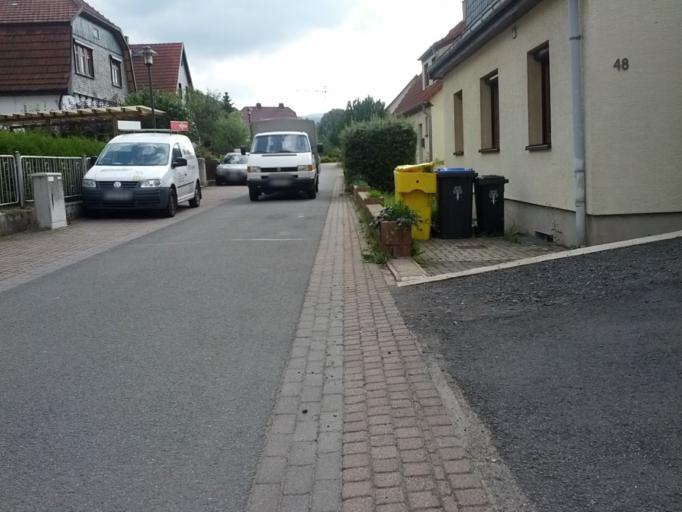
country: DE
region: Thuringia
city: Thal
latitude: 50.9359
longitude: 10.3947
